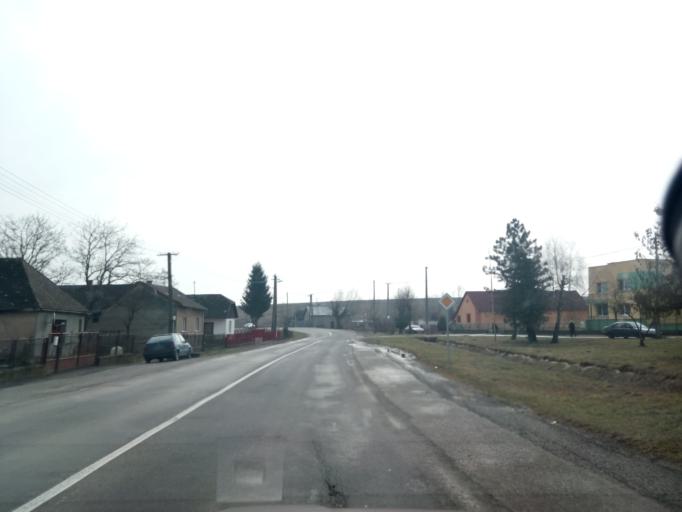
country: SK
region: Kosicky
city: Secovce
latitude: 48.6133
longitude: 21.6108
